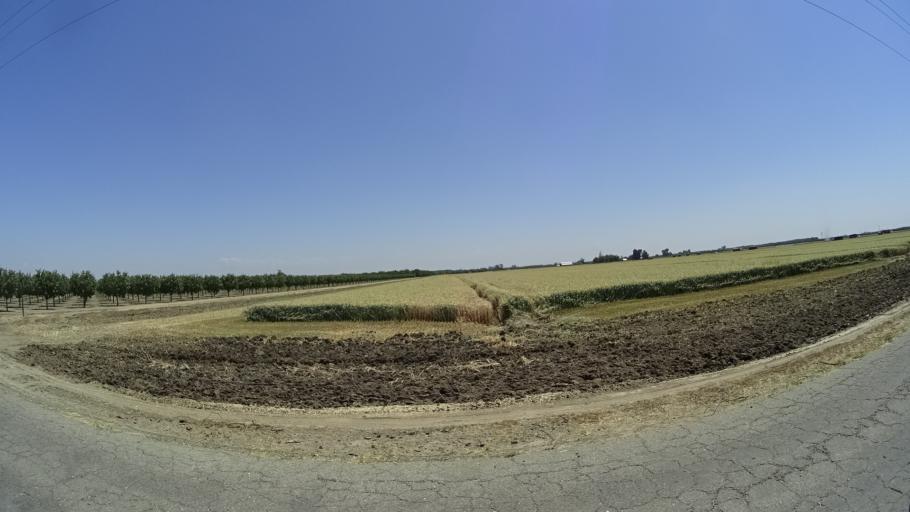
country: US
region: California
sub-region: Fresno County
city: Laton
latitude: 36.3944
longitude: -119.7268
